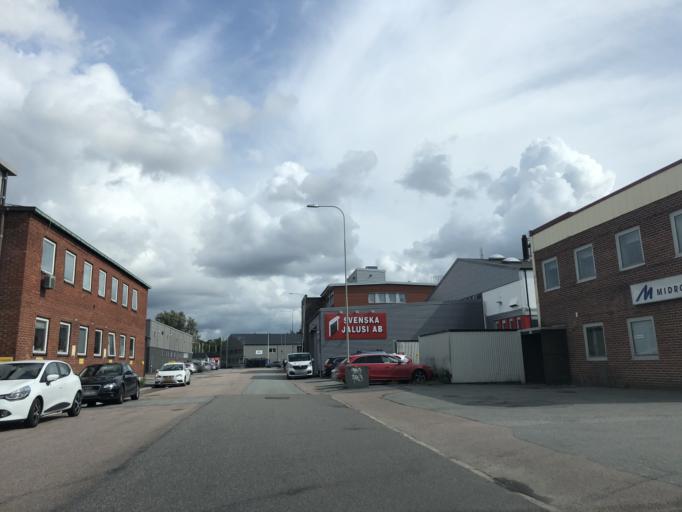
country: SE
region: Vaestra Goetaland
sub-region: Goteborg
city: Majorna
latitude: 57.7079
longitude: 11.8842
